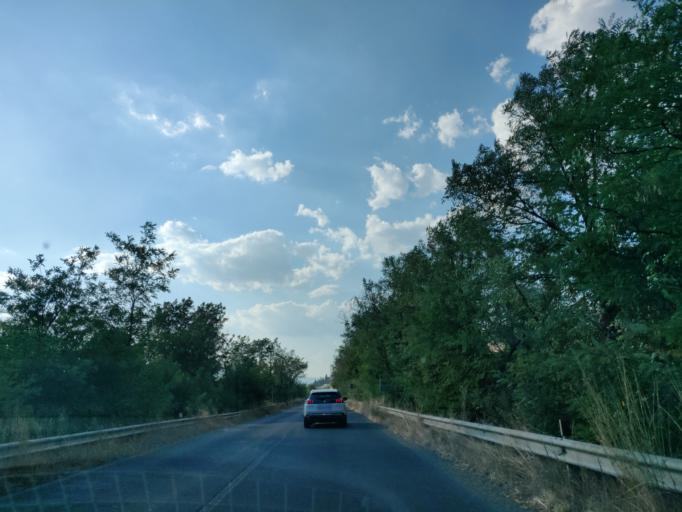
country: IT
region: Latium
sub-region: Provincia di Viterbo
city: Proceno
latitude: 42.7722
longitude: 11.8513
